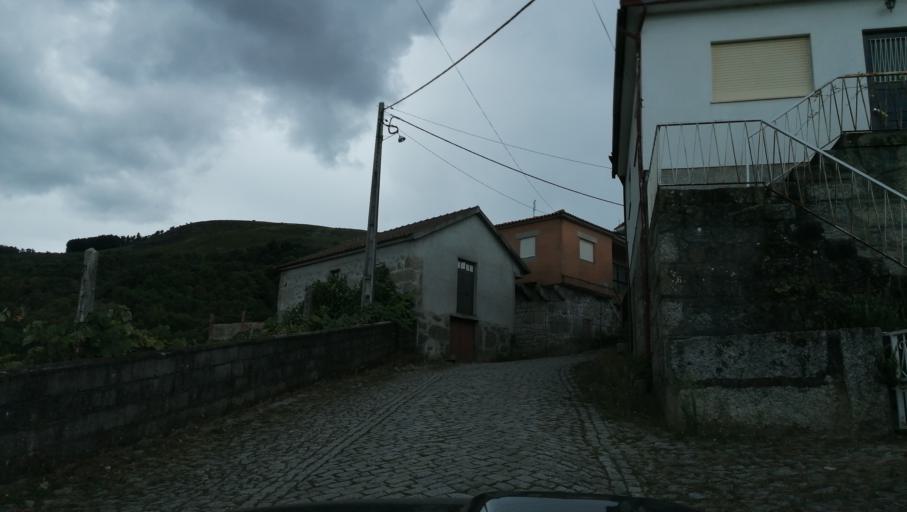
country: PT
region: Vila Real
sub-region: Vila Pouca de Aguiar
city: Vila Pouca de Aguiar
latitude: 41.5619
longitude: -7.6550
